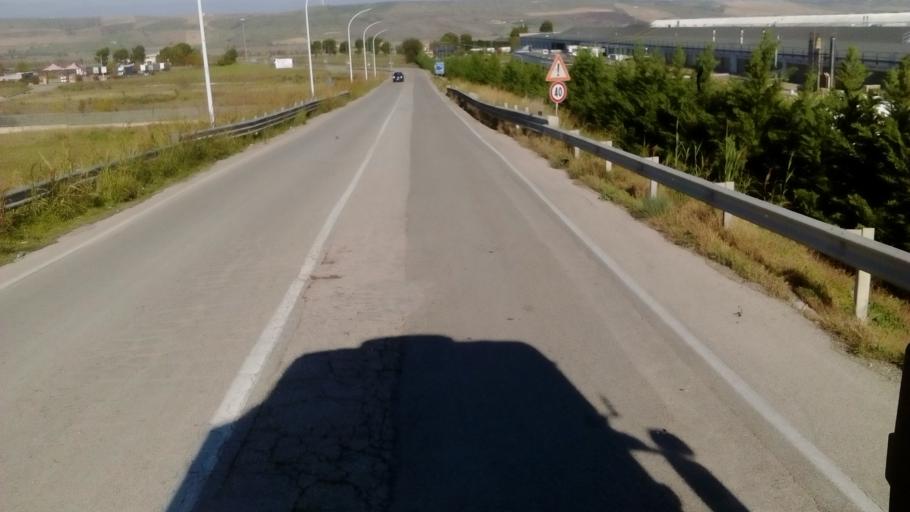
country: IT
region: Basilicate
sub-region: Provincia di Potenza
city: Melfi
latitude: 41.0725
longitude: 15.6907
